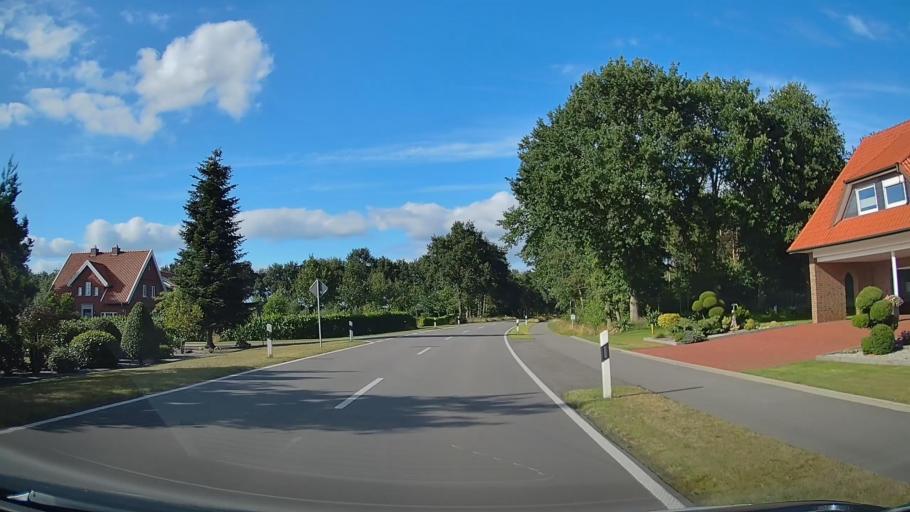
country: DE
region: Lower Saxony
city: Bosel
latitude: 52.9492
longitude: 7.8979
